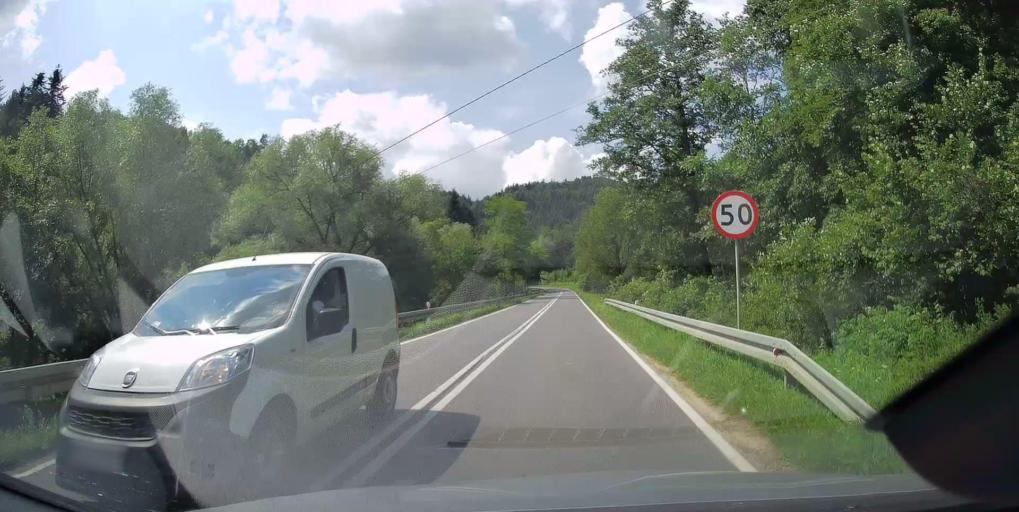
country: PL
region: Lesser Poland Voivodeship
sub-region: Powiat tarnowski
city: Zakliczyn
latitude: 49.8168
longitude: 20.7979
